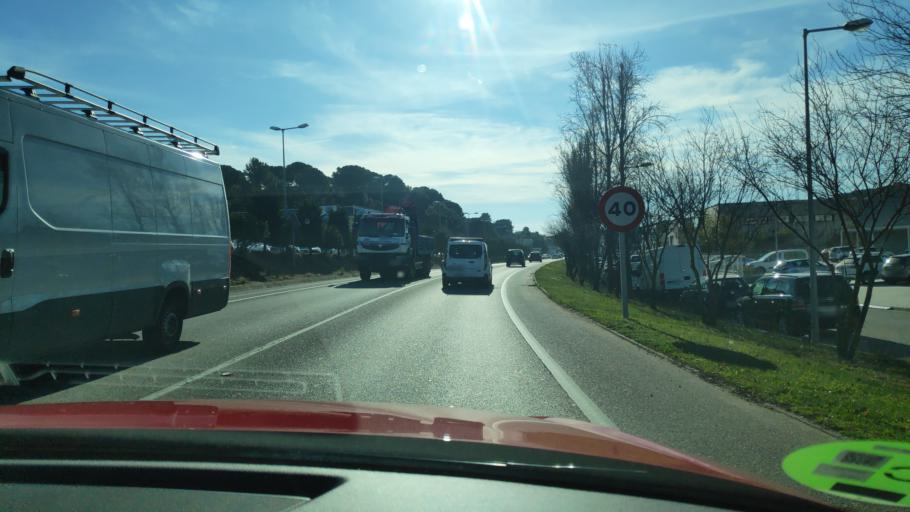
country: ES
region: Catalonia
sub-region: Provincia de Girona
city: Lloret de Mar
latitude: 41.7134
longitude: 2.8314
